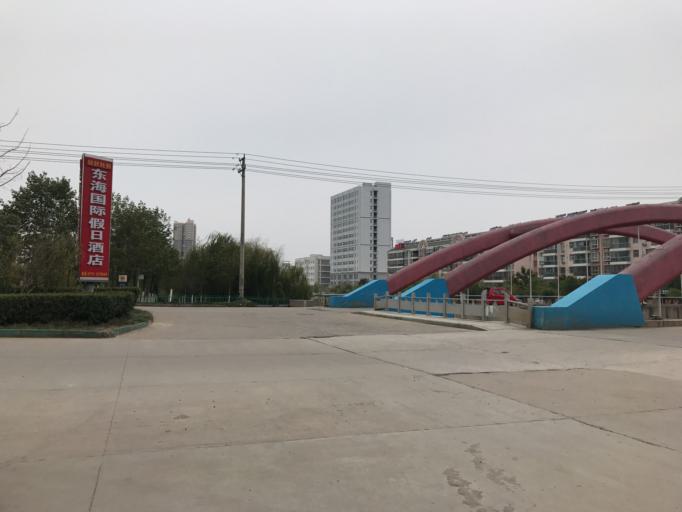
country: CN
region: Hubei
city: Anlu
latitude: 31.2700
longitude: 113.7048
